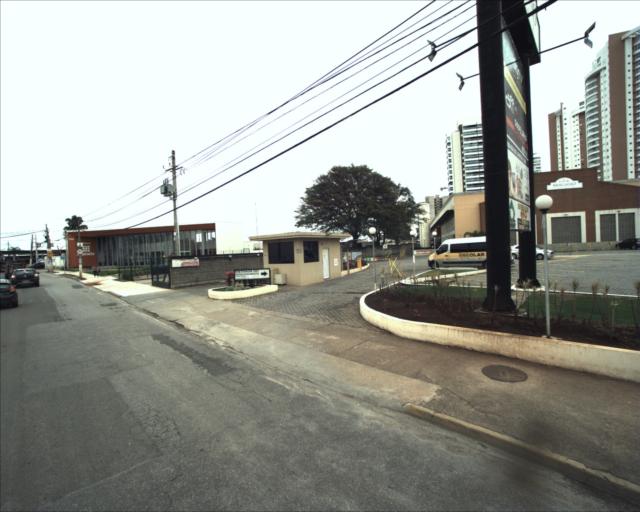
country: BR
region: Sao Paulo
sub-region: Votorantim
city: Votorantim
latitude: -23.5397
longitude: -47.4665
